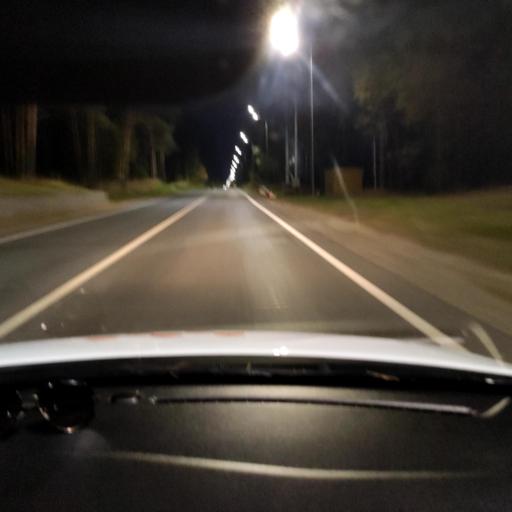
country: RU
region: Tatarstan
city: Verkhniy Uslon
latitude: 55.6370
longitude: 49.0571
